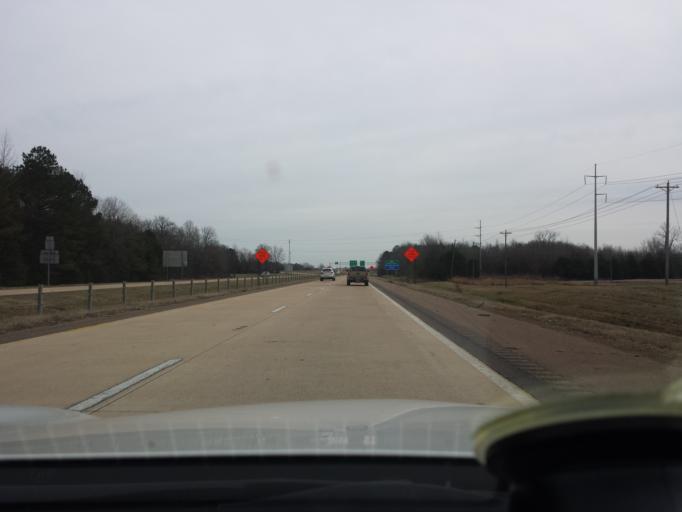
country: US
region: Mississippi
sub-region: Oktibbeha County
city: Starkville
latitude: 33.4774
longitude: -88.7700
